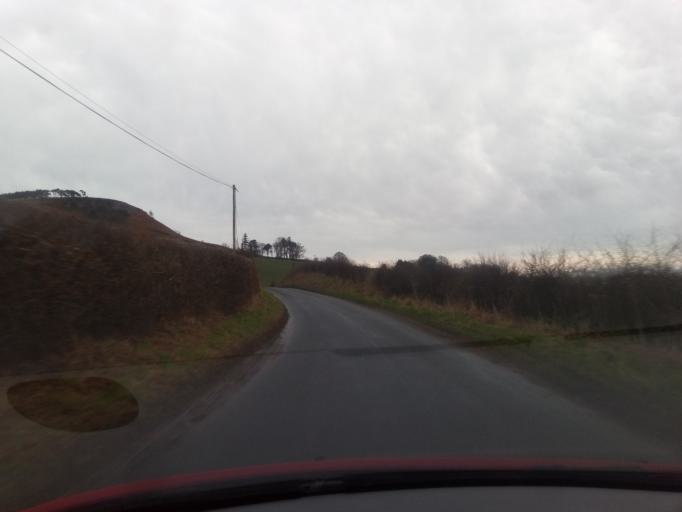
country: GB
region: England
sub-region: Northumberland
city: Whittingham
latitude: 55.4914
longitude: -1.9000
